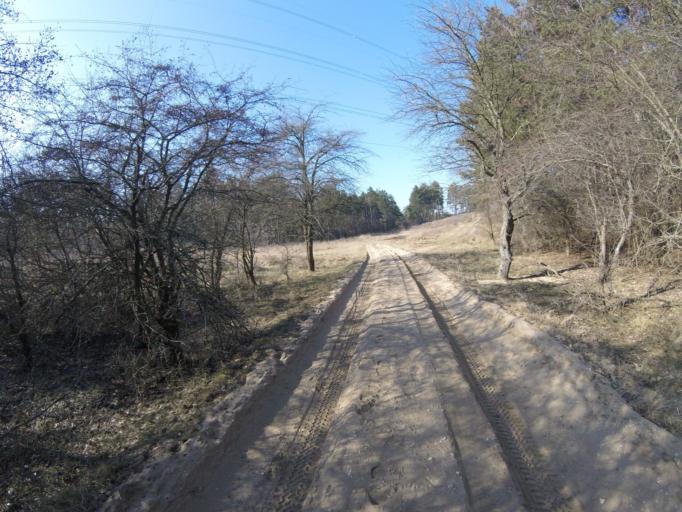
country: HU
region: Komarom-Esztergom
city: Oroszlany
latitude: 47.4589
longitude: 18.3607
